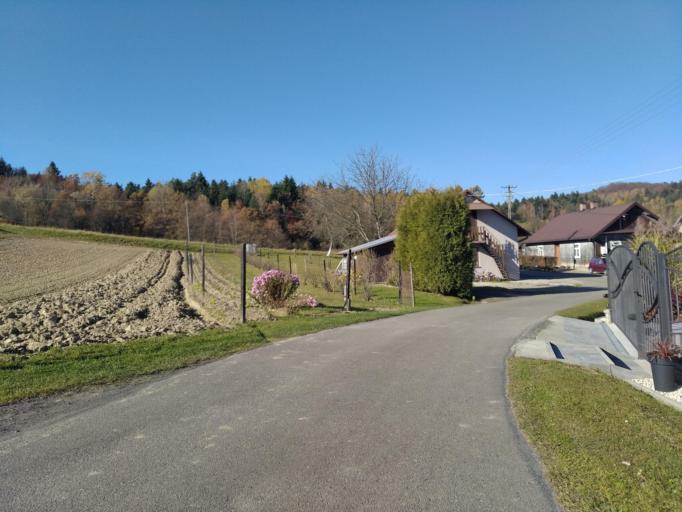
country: PL
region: Subcarpathian Voivodeship
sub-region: Powiat strzyzowski
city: Frysztak
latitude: 49.8506
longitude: 21.6032
